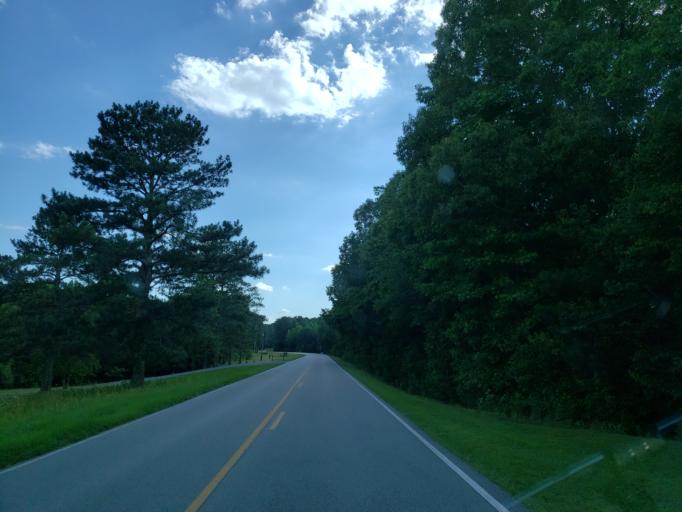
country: US
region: Georgia
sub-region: Polk County
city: Rockmart
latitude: 33.9014
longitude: -85.0792
